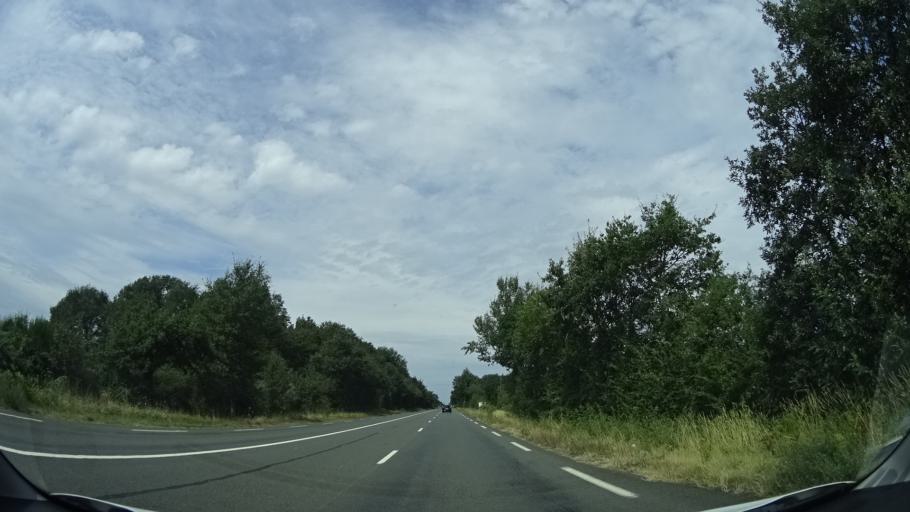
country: FR
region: Pays de la Loire
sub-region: Departement de la Sarthe
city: Bazouges-sur-le-Loir
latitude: 47.7597
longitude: -0.1789
